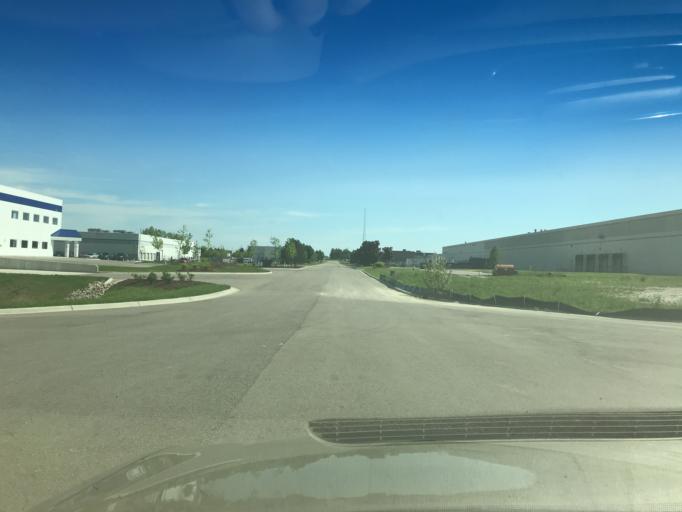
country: US
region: Michigan
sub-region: Eaton County
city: Waverly
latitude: 42.7076
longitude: -84.6673
